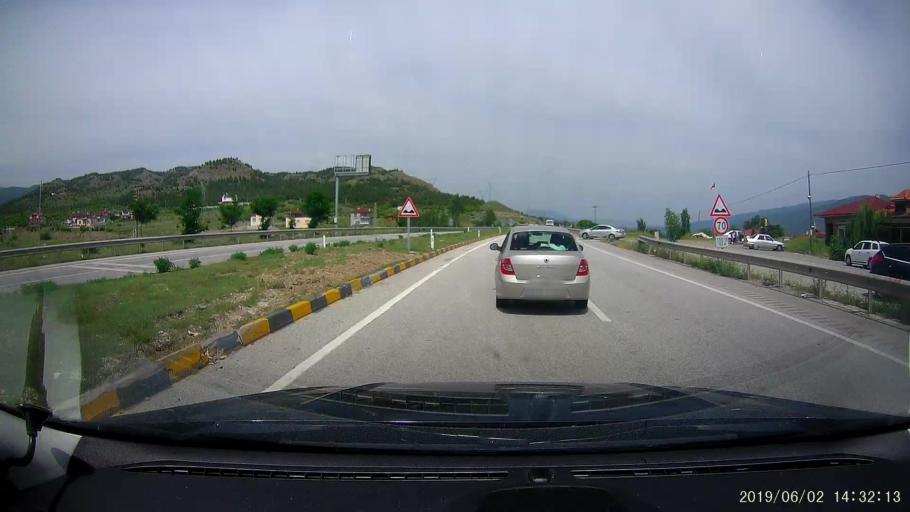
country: TR
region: Kastamonu
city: Tosya
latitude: 41.0240
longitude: 34.1481
